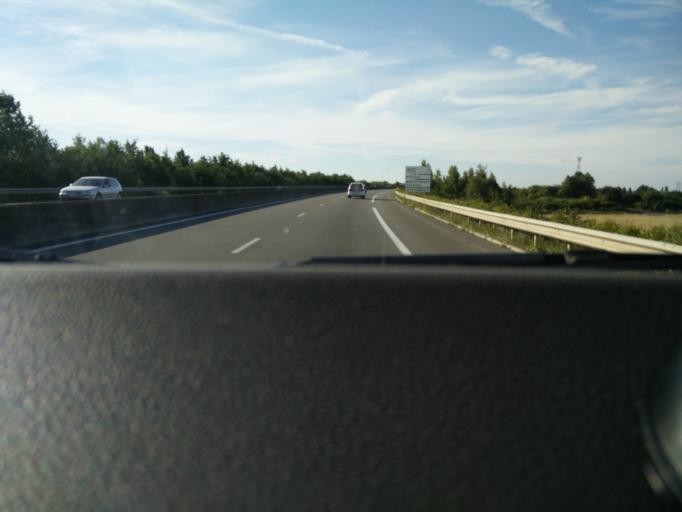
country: FR
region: Nord-Pas-de-Calais
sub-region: Departement du Nord
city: Somain
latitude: 50.3513
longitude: 3.2639
